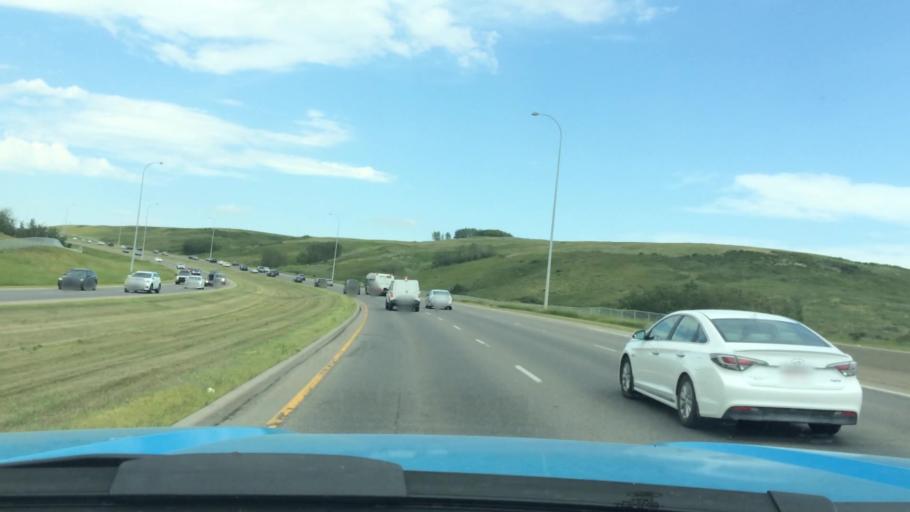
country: CA
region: Alberta
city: Calgary
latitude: 51.1142
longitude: -114.1350
